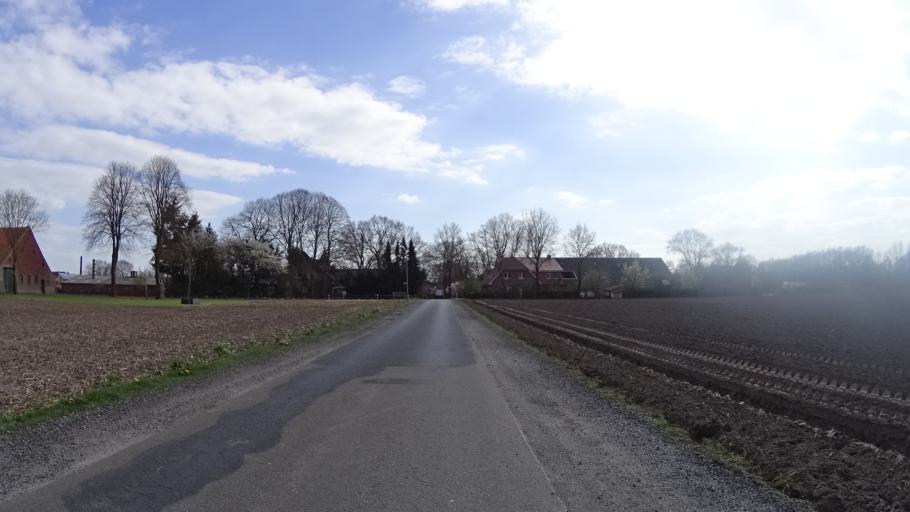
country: DE
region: Lower Saxony
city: Lehe
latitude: 53.0323
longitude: 7.3216
